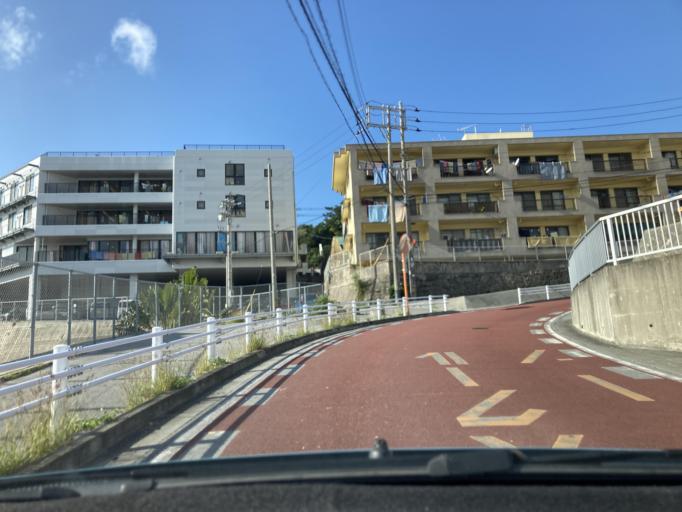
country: JP
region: Okinawa
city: Tomigusuku
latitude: 26.1821
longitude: 127.6825
